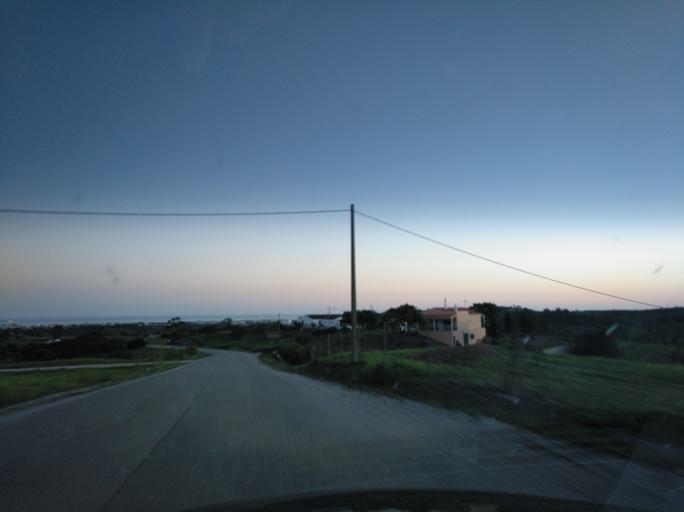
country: PT
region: Faro
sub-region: Vila Real de Santo Antonio
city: Monte Gordo
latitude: 37.2098
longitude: -7.5200
